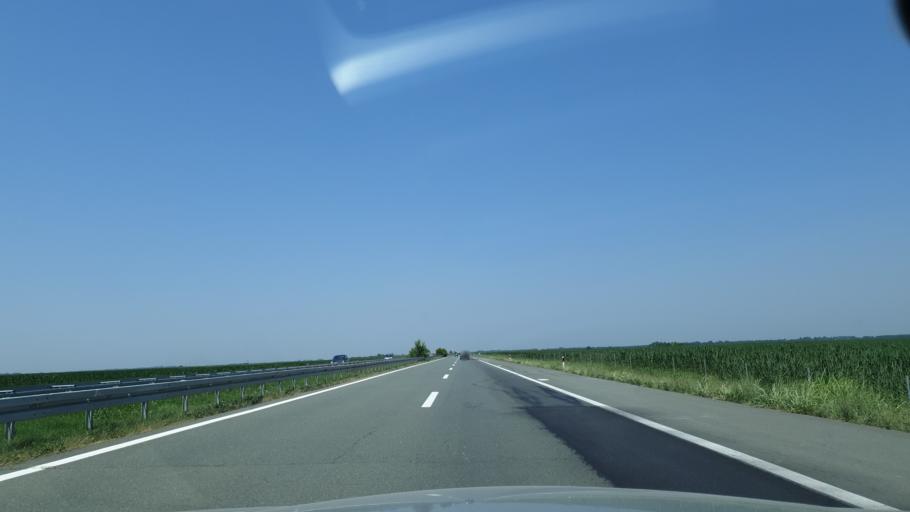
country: RS
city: Zmajevo
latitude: 45.4806
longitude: 19.7290
